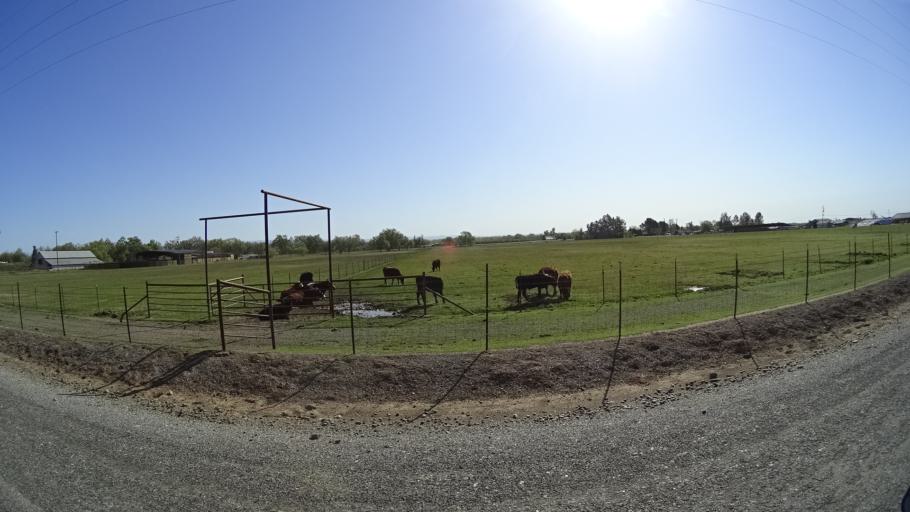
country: US
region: California
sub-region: Glenn County
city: Hamilton City
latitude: 39.7835
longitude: -122.0519
